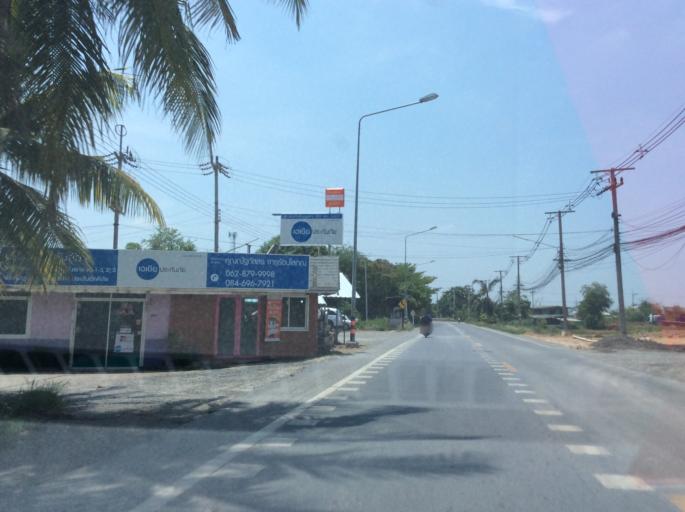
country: TH
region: Pathum Thani
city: Ban Rangsit
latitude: 14.0171
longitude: 100.7796
